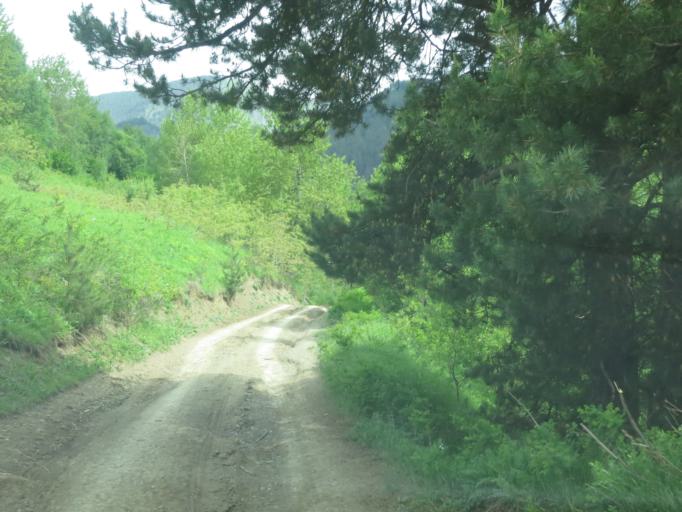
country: RU
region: Chechnya
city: Itum-Kali
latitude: 42.3647
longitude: 45.6427
